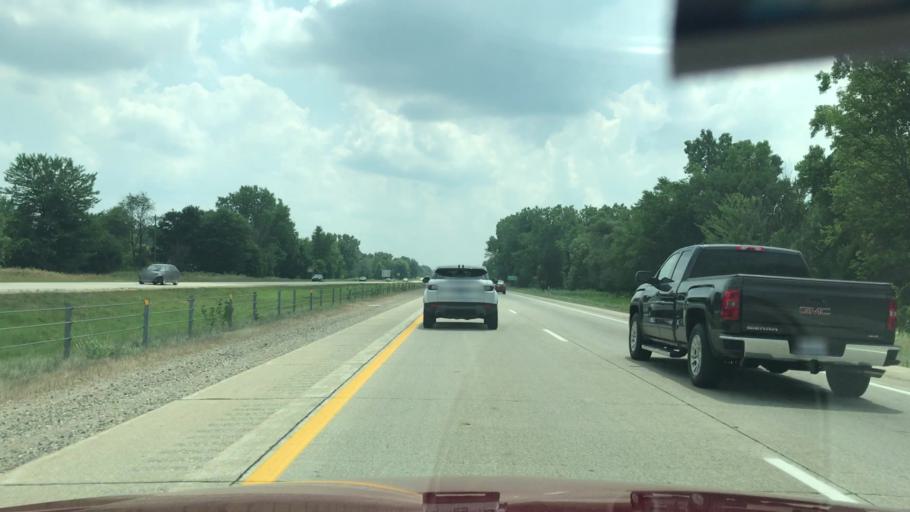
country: US
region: Michigan
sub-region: Allegan County
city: Plainwell
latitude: 42.4234
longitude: -85.6607
